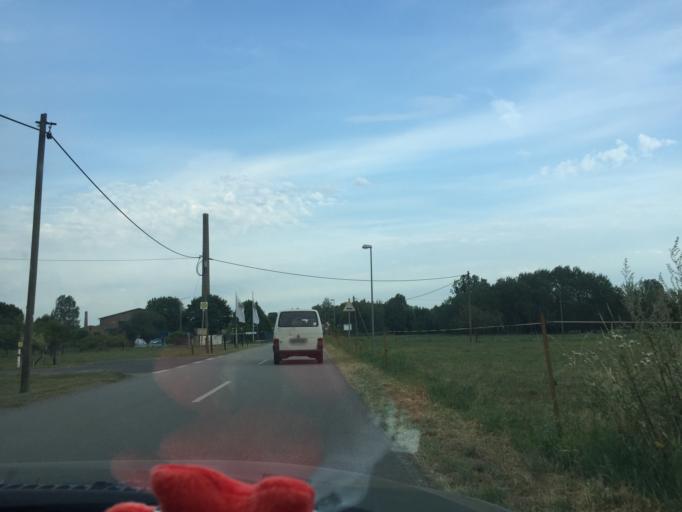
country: DE
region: Brandenburg
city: Zehdenick
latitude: 53.0294
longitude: 13.3005
